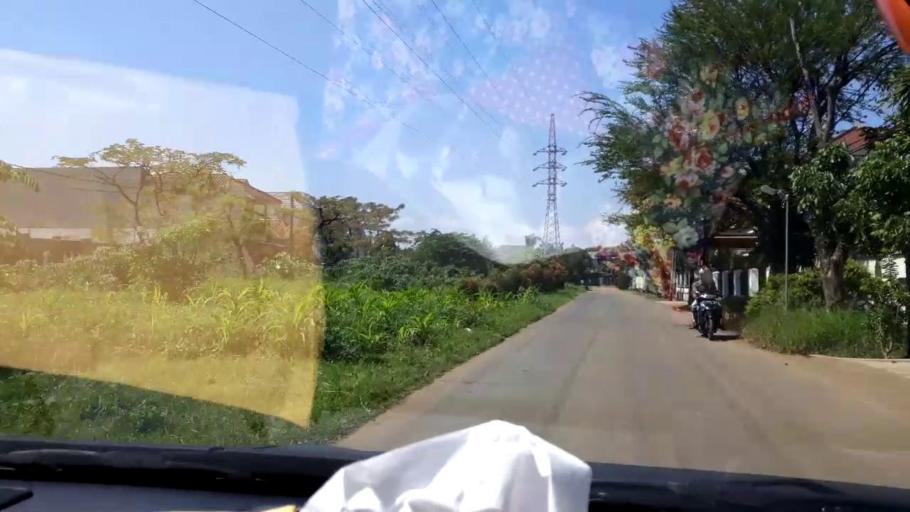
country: ID
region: West Java
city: Bandung
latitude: -6.9228
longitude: 107.6730
